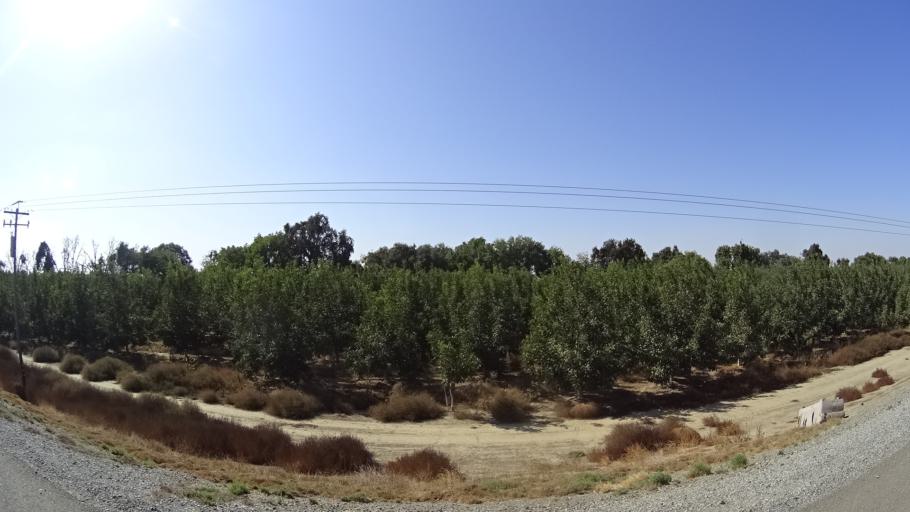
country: US
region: California
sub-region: Yolo County
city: West Sacramento
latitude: 38.6109
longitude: -121.5618
